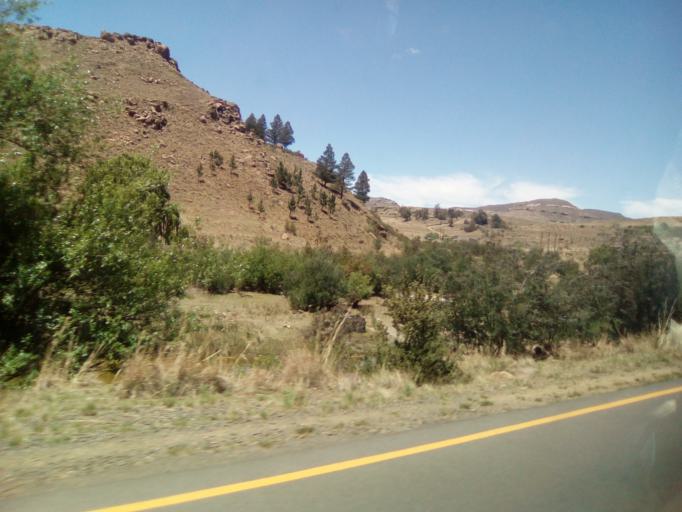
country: LS
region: Qacha's Nek
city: Qacha's Nek
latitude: -30.1022
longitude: 28.6565
